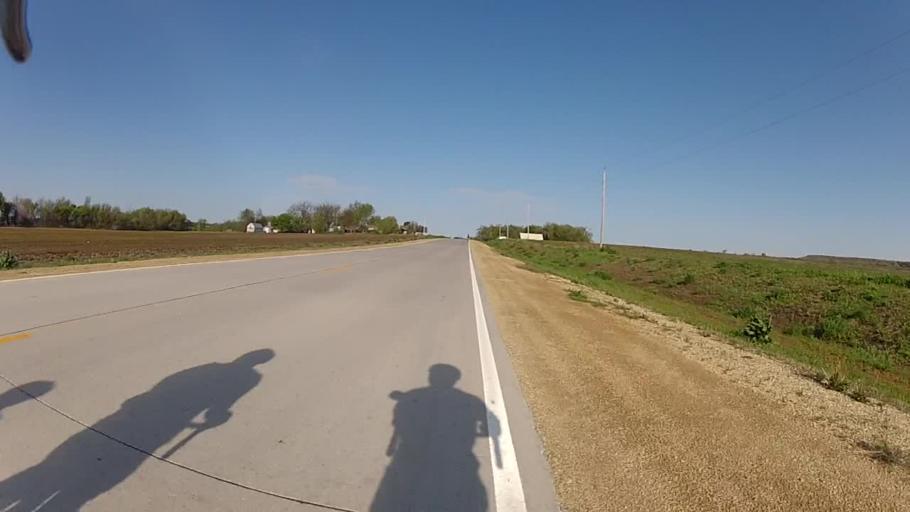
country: US
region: Kansas
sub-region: Riley County
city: Ogden
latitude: 39.1532
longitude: -96.6739
